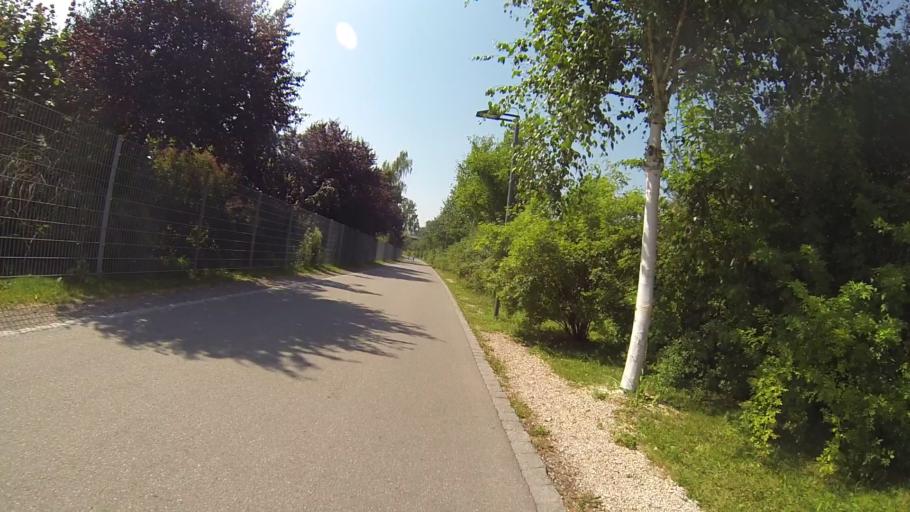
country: DE
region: Baden-Wuerttemberg
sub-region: Regierungsbezirk Stuttgart
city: Heidenheim an der Brenz
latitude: 48.6899
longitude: 10.1563
